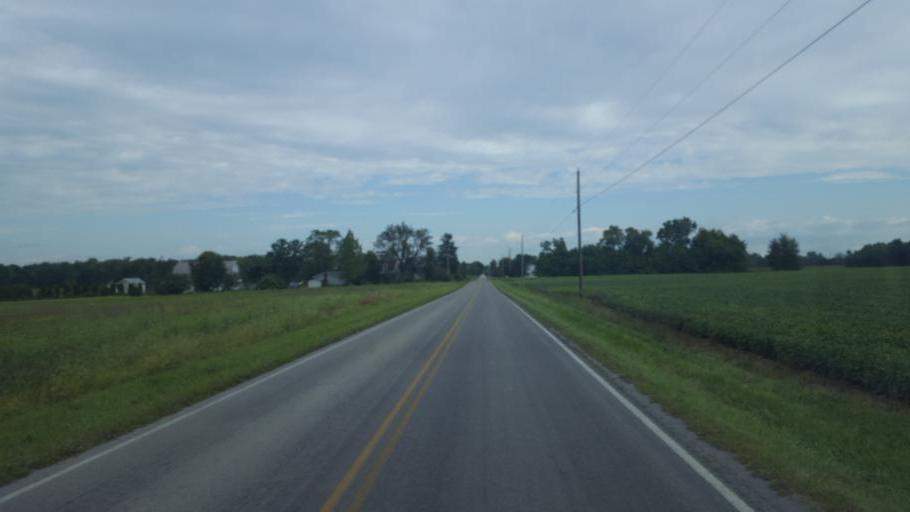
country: US
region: Ohio
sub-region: Wyandot County
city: Upper Sandusky
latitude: 40.9355
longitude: -83.1698
